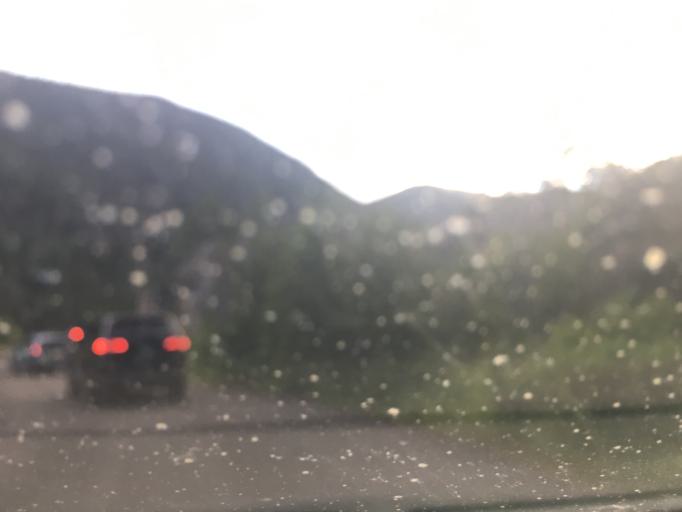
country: US
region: Colorado
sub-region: Larimer County
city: Estes Park
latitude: 40.4128
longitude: -105.6490
